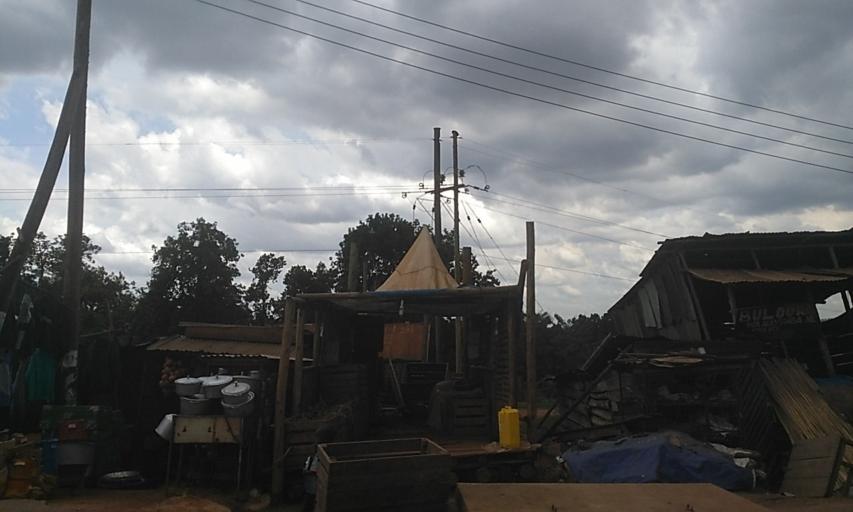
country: UG
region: Central Region
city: Kampala Central Division
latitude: 0.3199
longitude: 32.5065
